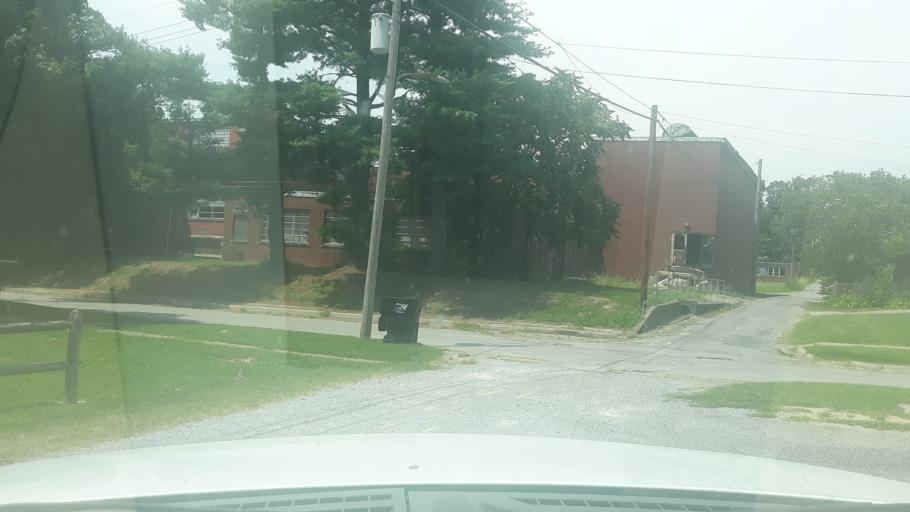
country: US
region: Illinois
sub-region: Saline County
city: Harrisburg
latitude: 37.7355
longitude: -88.5427
